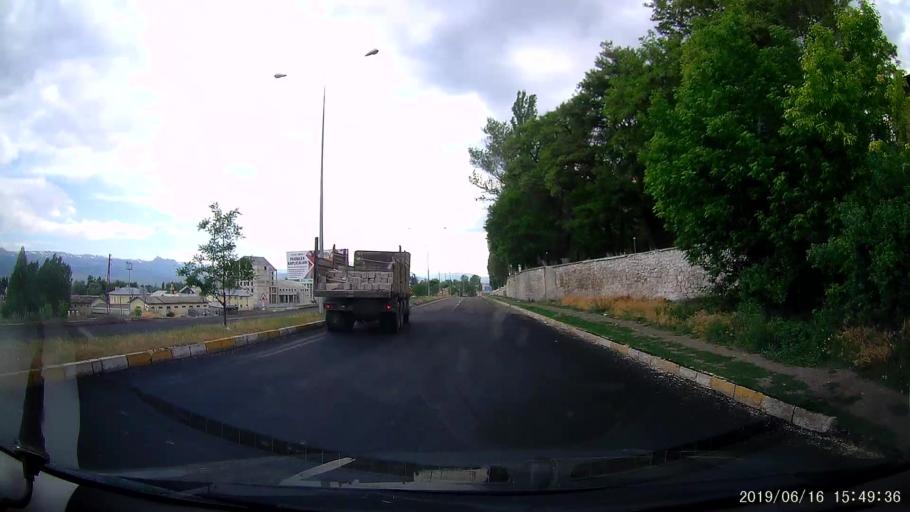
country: TR
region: Erzurum
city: Pasinler
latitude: 39.9783
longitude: 41.6851
